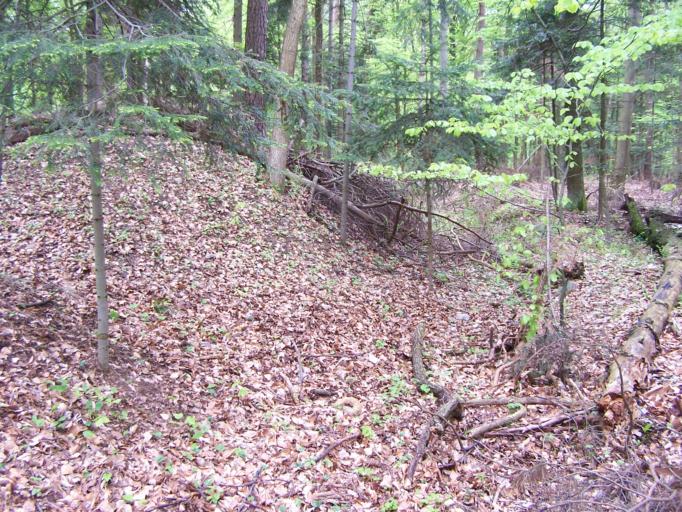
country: PL
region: Swietokrzyskie
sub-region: Powiat starachowicki
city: Brody
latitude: 51.0650
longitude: 21.1574
